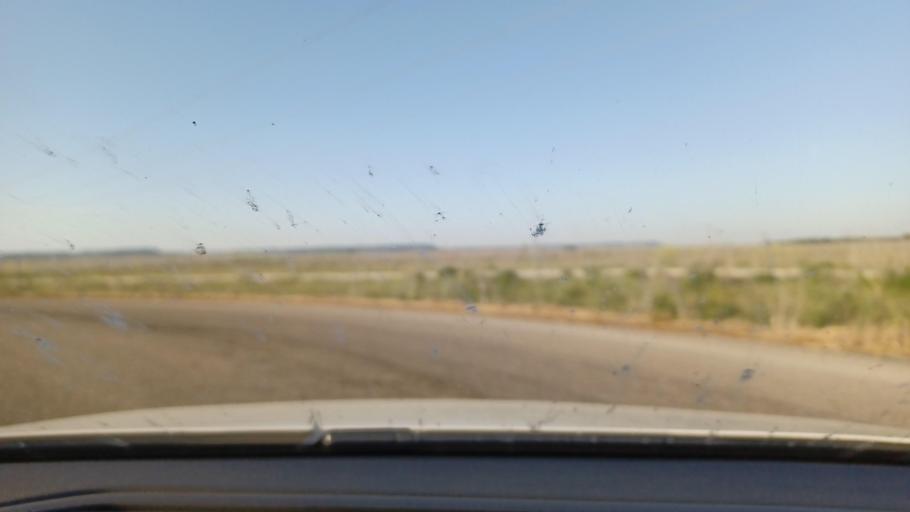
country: ES
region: Castille and Leon
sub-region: Provincia de Valladolid
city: Aldea de San Miguel
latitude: 41.4892
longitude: -4.6168
